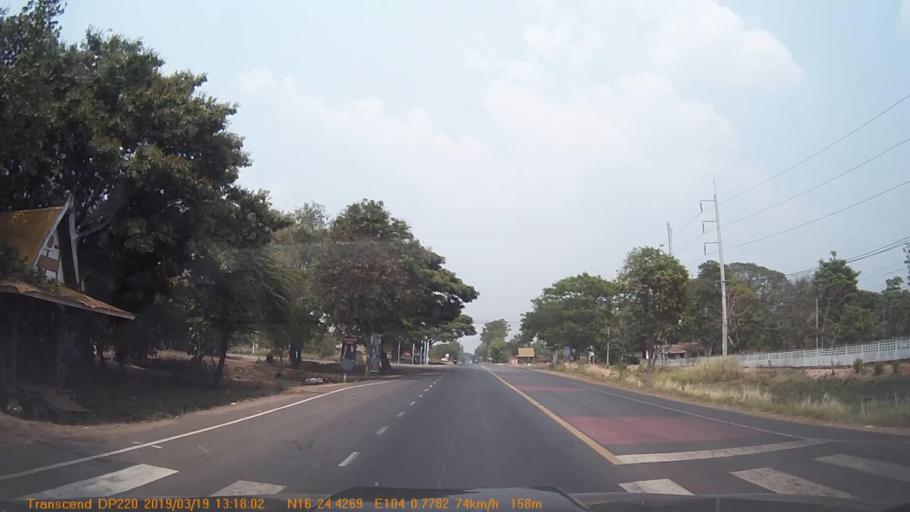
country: TH
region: Roi Et
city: Waeng
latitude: 16.4075
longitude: 104.0131
